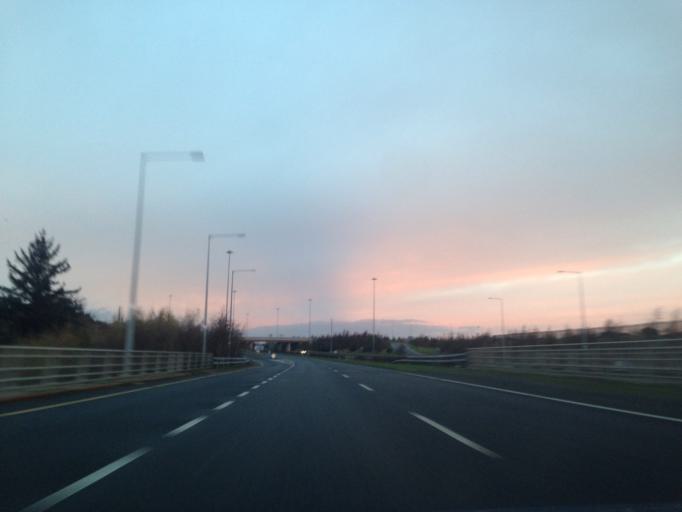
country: IE
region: Leinster
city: Loughlinstown
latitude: 53.2390
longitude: -6.1467
